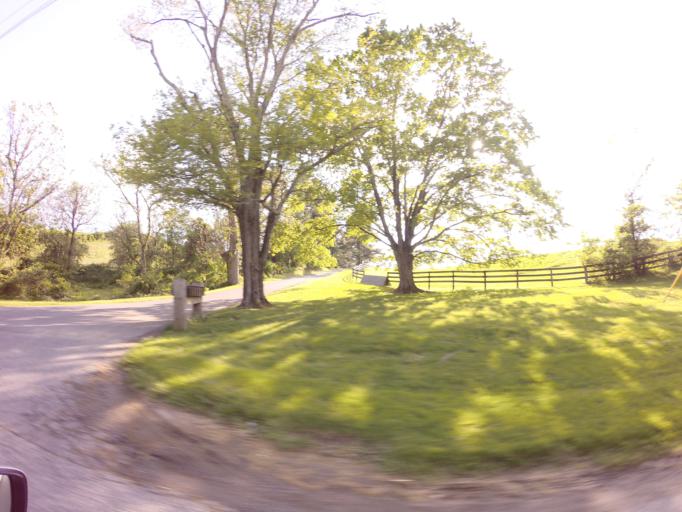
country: US
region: Maryland
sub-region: Baltimore County
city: Hunt Valley
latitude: 39.5157
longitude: -76.7172
